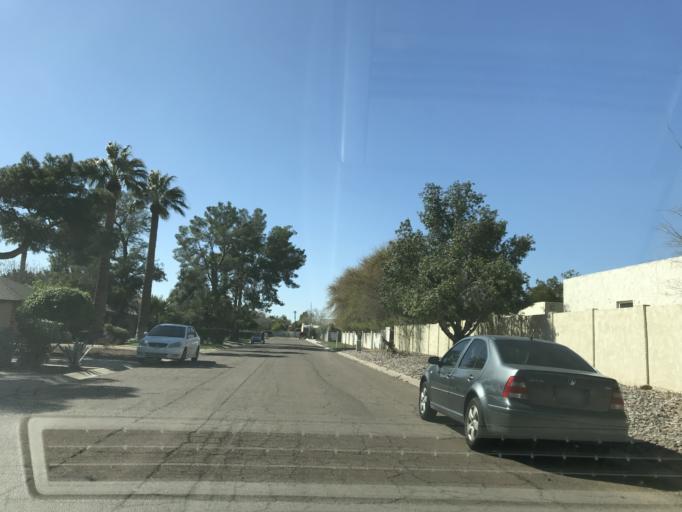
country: US
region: Arizona
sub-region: Maricopa County
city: Phoenix
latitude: 33.5146
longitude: -112.0693
